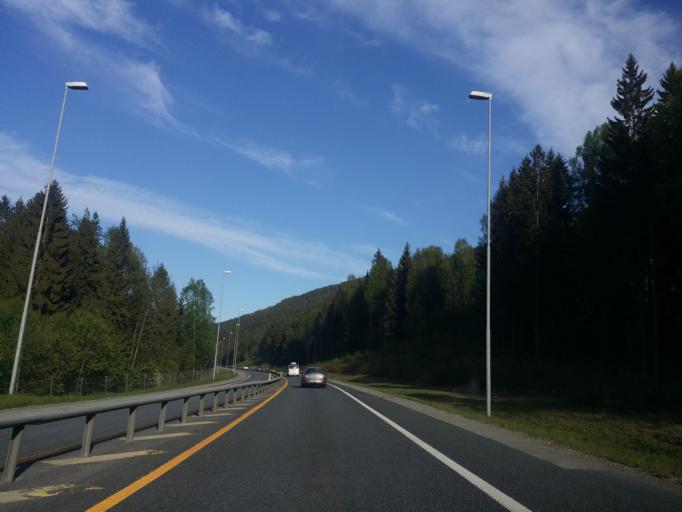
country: NO
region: Buskerud
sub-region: Nedre Eiker
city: Mjondalen
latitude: 59.7435
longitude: 10.0743
